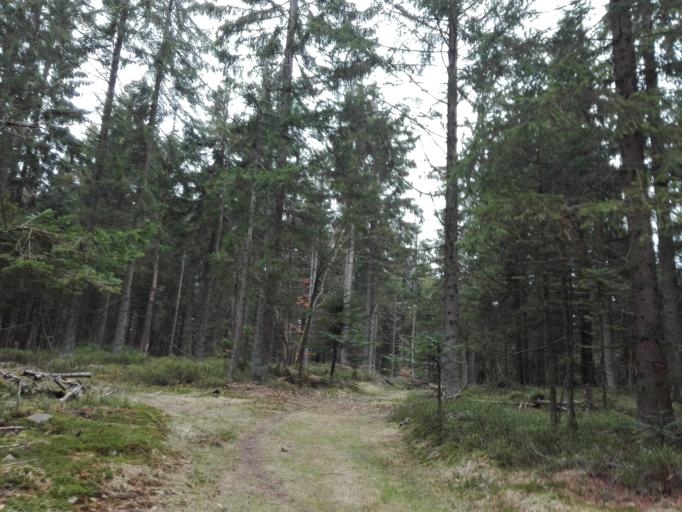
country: AT
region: Upper Austria
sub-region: Politischer Bezirk Rohrbach
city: Aigen im Muehlkreis
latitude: 48.6951
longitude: 13.9579
